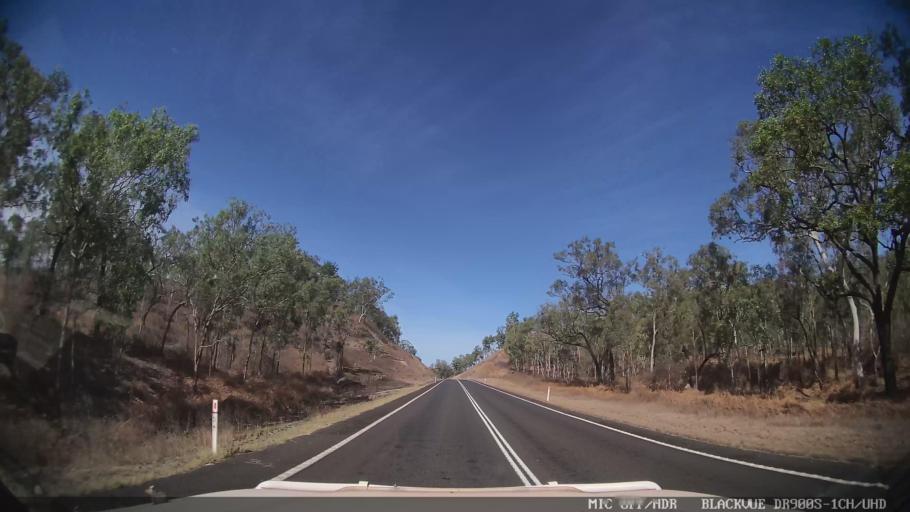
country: AU
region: Queensland
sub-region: Cook
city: Cooktown
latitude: -15.7888
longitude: 144.9430
